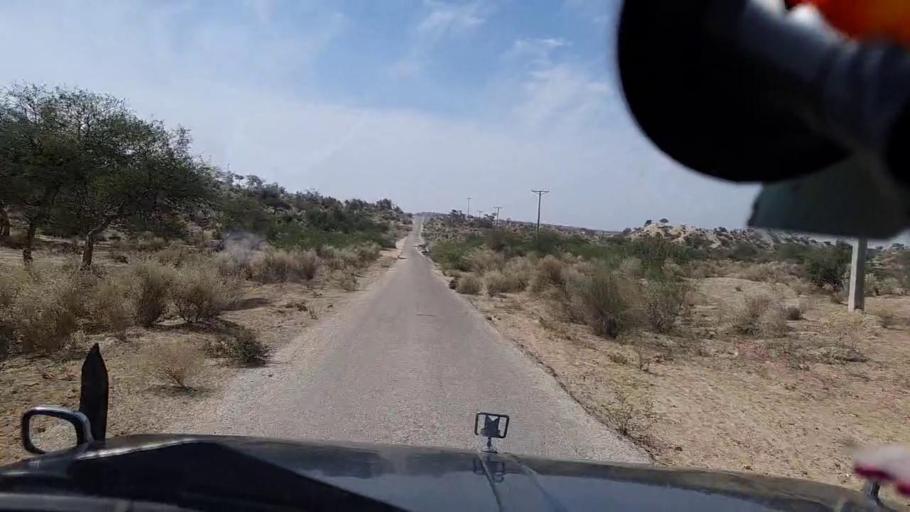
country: PK
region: Sindh
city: Diplo
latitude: 24.3820
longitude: 69.5857
